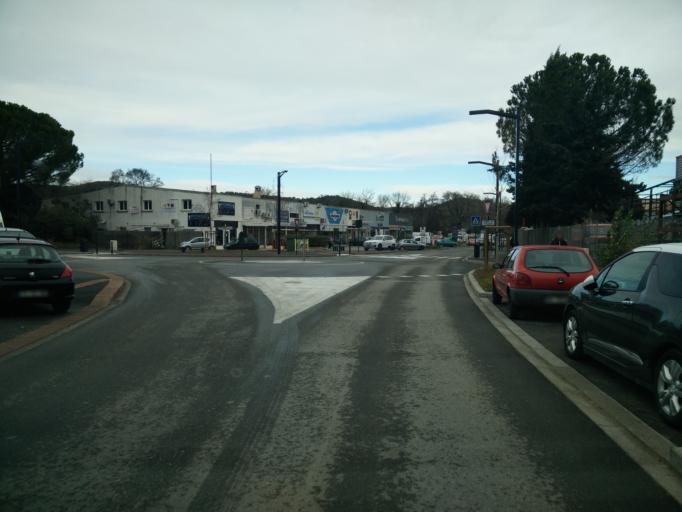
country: FR
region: Provence-Alpes-Cote d'Azur
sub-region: Departement du Var
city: Brignoles
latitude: 43.4049
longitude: 6.0538
